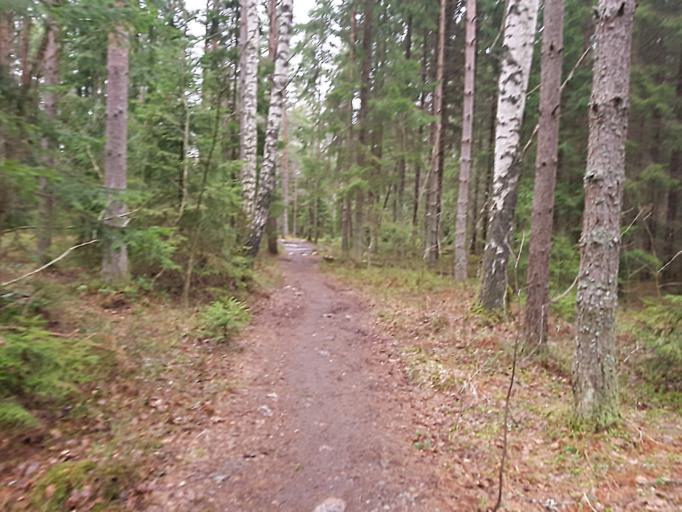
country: FI
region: Uusimaa
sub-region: Helsinki
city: Helsinki
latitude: 60.2613
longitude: 24.9211
